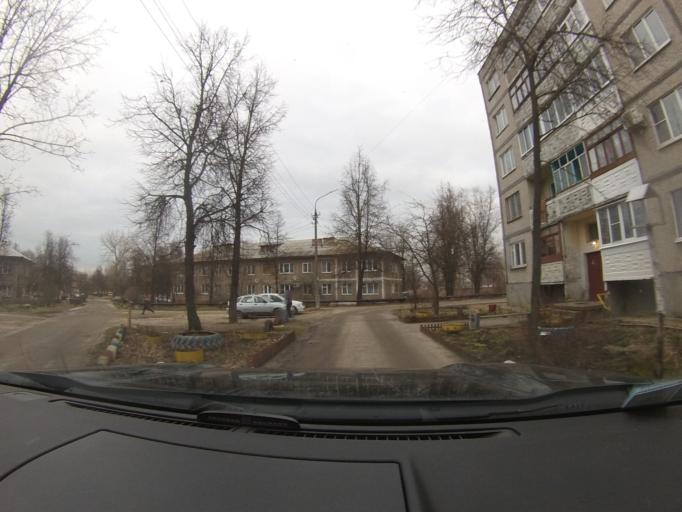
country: RU
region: Moskovskaya
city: Lopatinskiy
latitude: 55.3205
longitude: 38.7031
